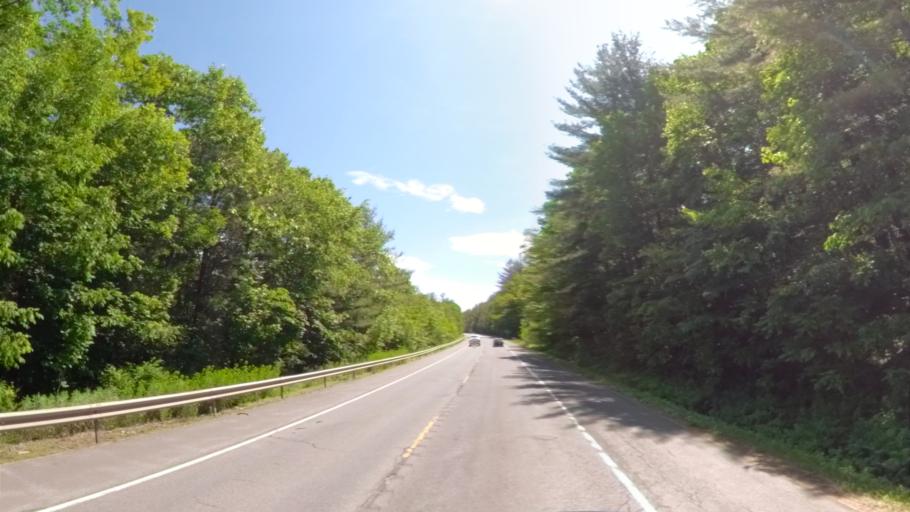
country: US
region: New York
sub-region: Ulster County
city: Shokan
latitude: 42.1151
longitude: -74.4199
